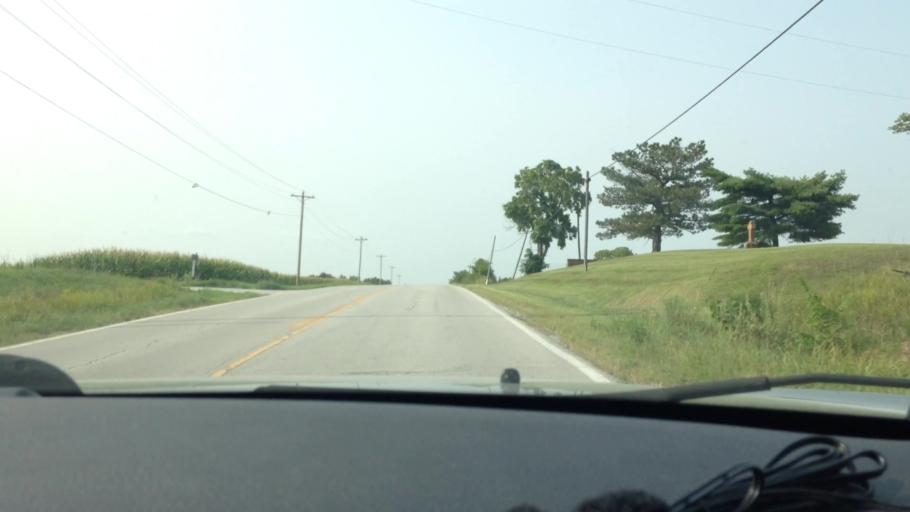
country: US
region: Missouri
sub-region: Platte County
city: Platte City
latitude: 39.4072
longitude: -94.7961
